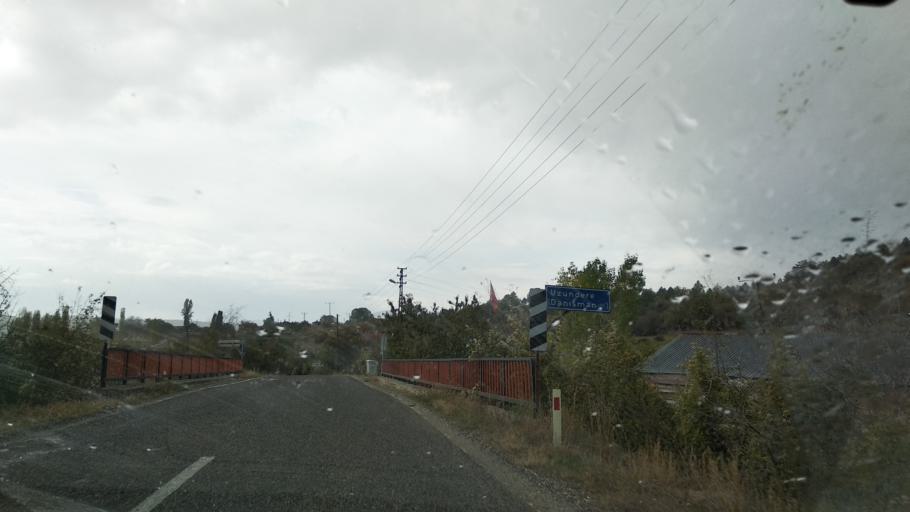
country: TR
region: Ankara
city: Nallihan
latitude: 40.3335
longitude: 31.4140
